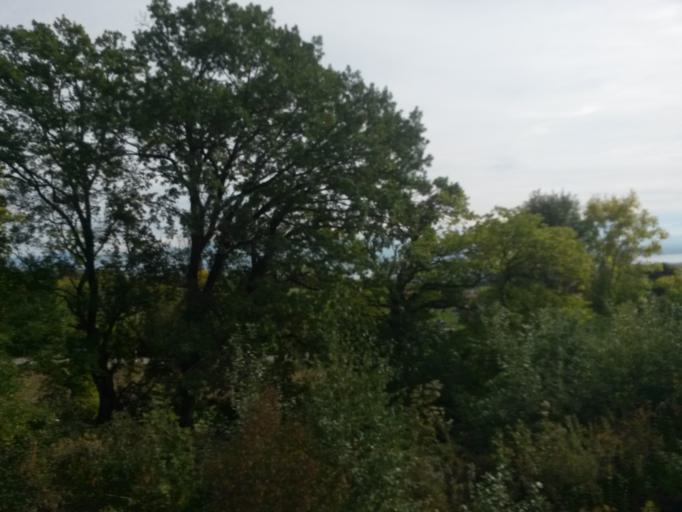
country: CH
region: Vaud
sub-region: Nyon District
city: Arzier
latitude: 46.4577
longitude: 6.2190
